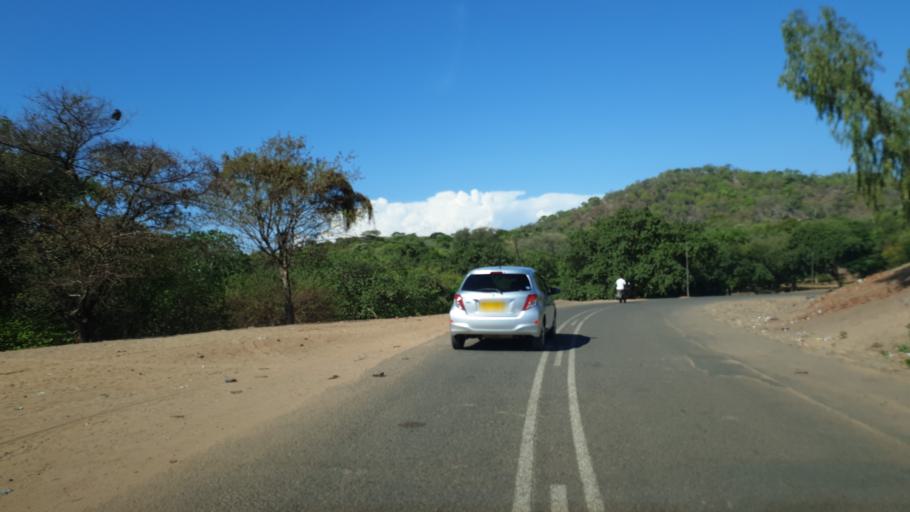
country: MW
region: Central Region
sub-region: Salima District
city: Salima
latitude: -13.7179
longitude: 34.6216
